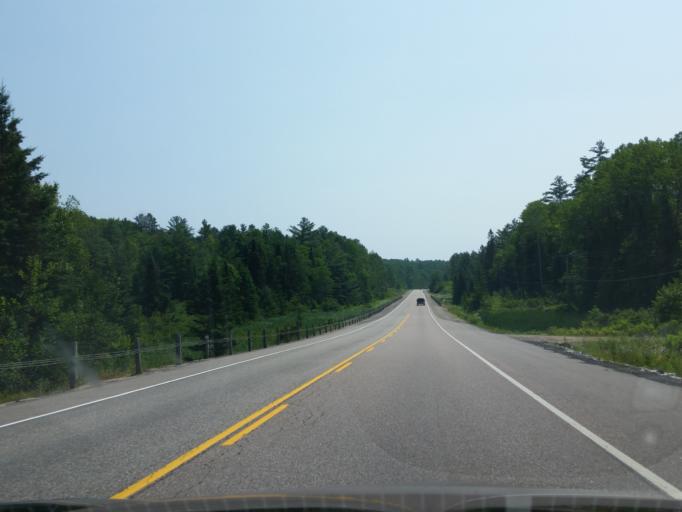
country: CA
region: Ontario
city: Deep River
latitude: 46.1820
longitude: -77.7372
